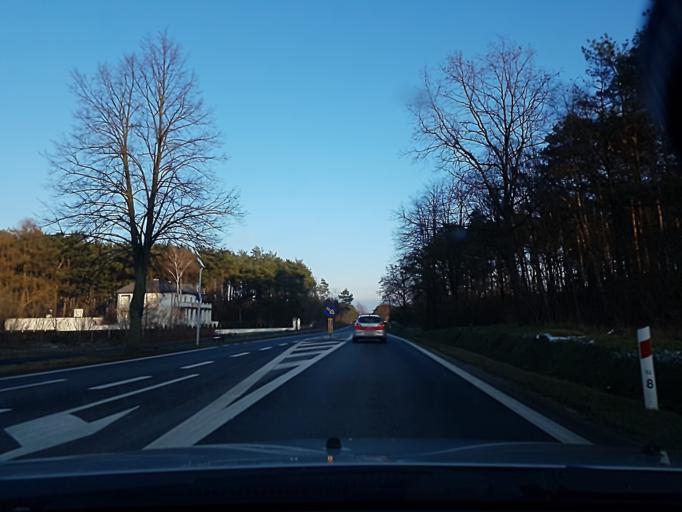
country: PL
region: Masovian Voivodeship
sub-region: Powiat plocki
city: Lack
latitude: 52.4524
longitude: 19.5431
